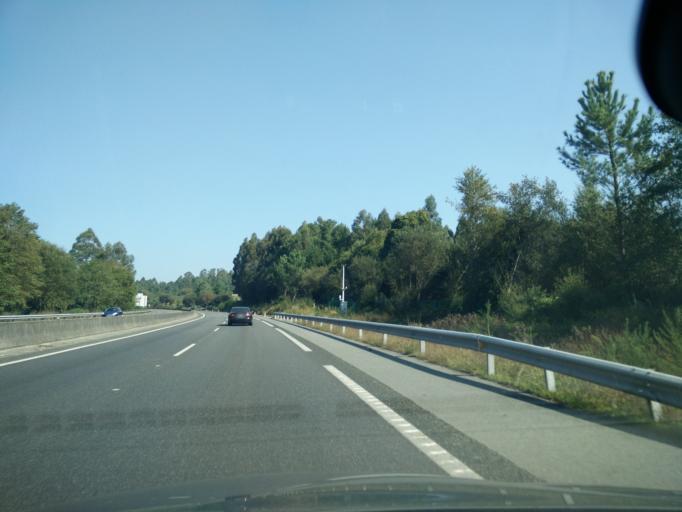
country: ES
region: Galicia
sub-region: Provincia da Coruna
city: Mino
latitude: 43.3824
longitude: -8.1788
